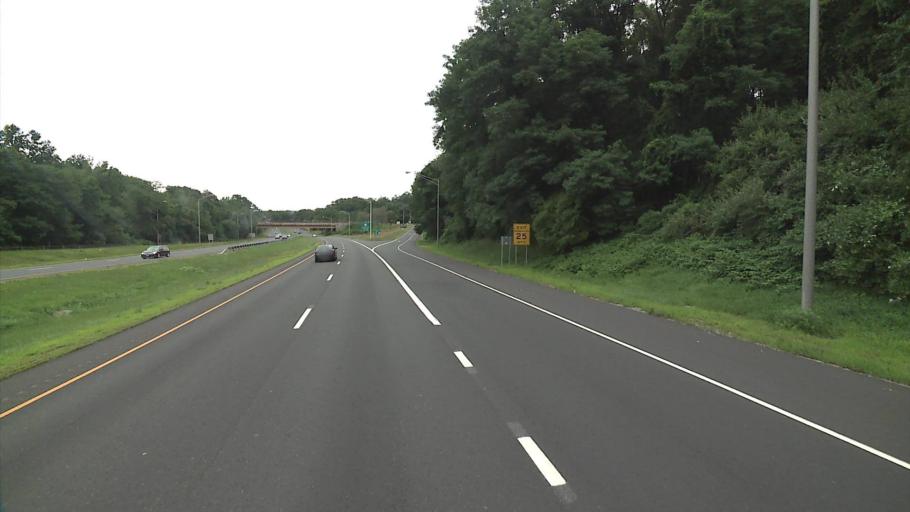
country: US
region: Connecticut
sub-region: Fairfield County
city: Shelton
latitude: 41.3019
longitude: -73.1010
